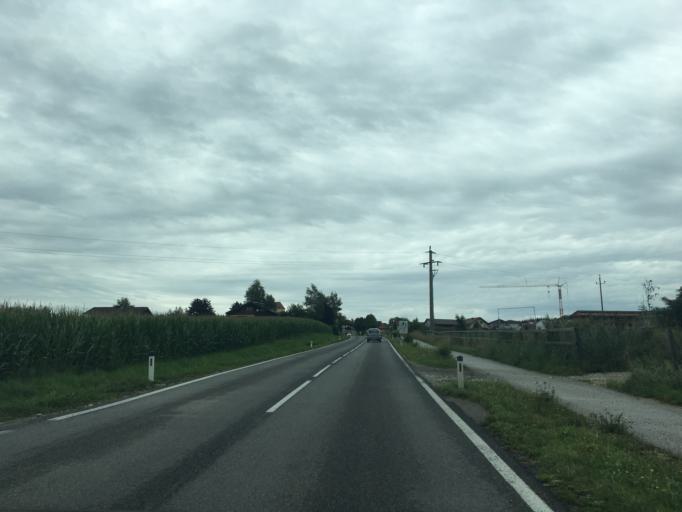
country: AT
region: Salzburg
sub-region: Politischer Bezirk Salzburg-Umgebung
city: Dorfbeuern
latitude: 48.0400
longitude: 12.9883
